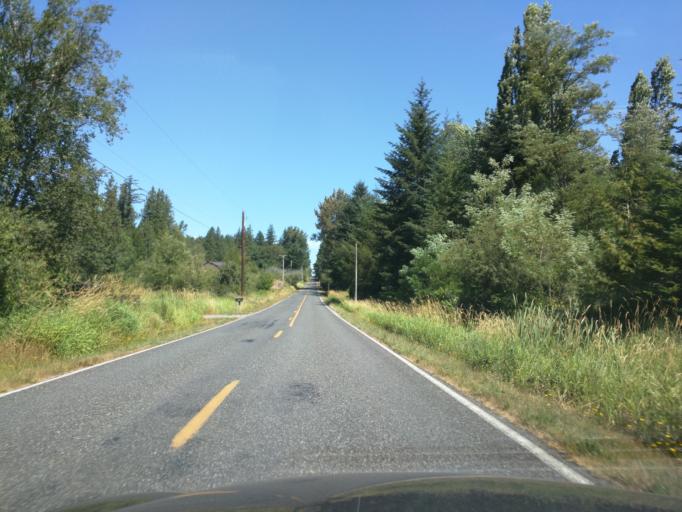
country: US
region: Washington
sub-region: Whatcom County
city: Geneva
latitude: 48.8169
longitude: -122.3989
